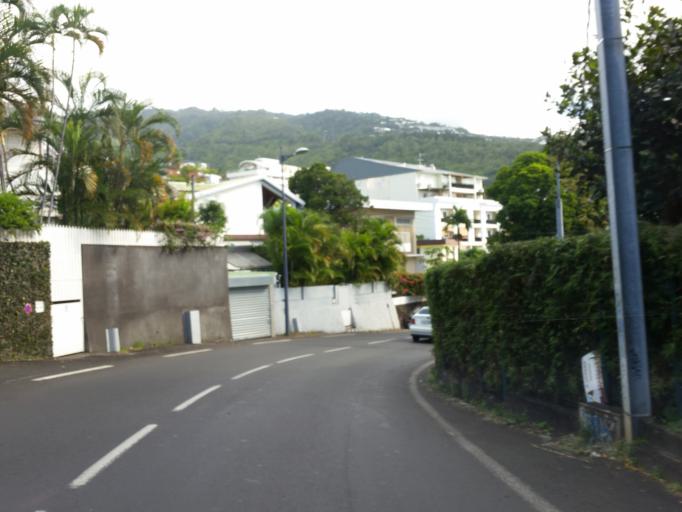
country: RE
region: Reunion
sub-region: Reunion
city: Saint-Denis
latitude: -20.8968
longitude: 55.4613
